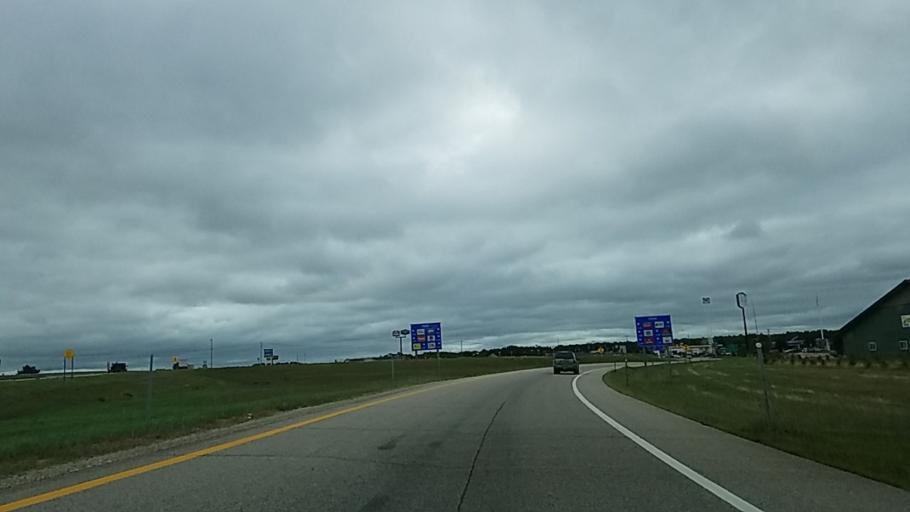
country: US
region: Michigan
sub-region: Otsego County
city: Gaylord
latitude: 45.0304
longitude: -84.6896
